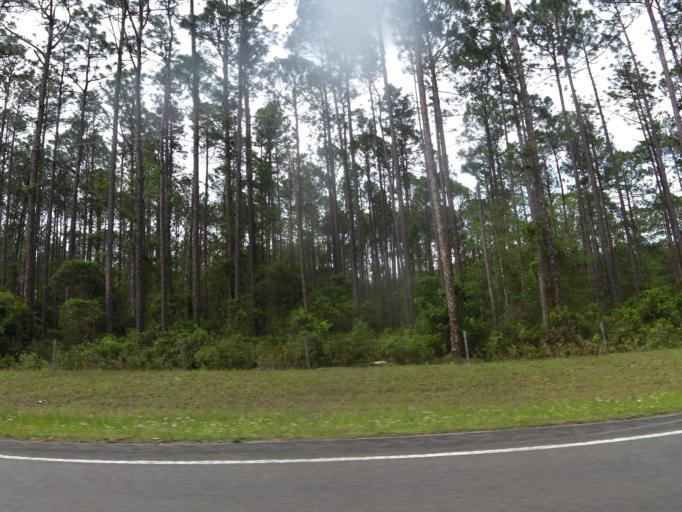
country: US
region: Florida
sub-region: Nassau County
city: Hilliard
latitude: 30.6963
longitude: -81.8012
